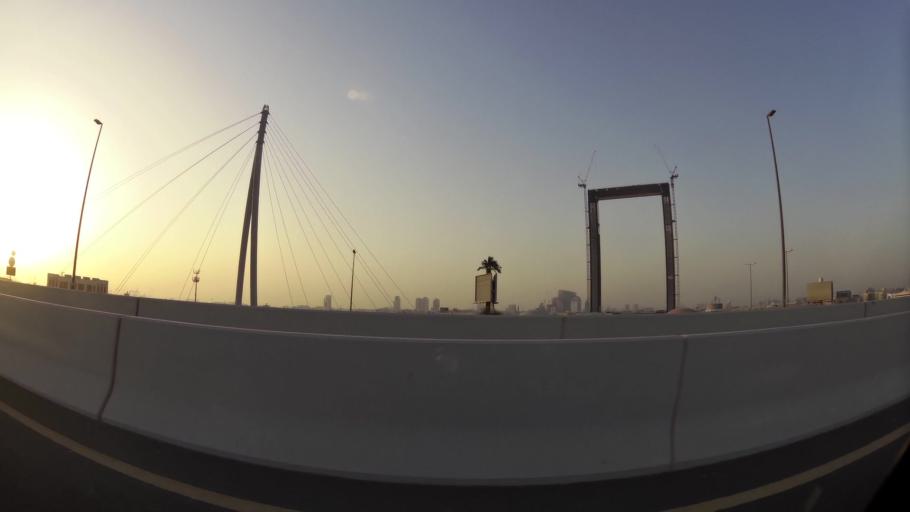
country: AE
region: Ash Shariqah
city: Sharjah
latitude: 25.2313
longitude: 55.2996
